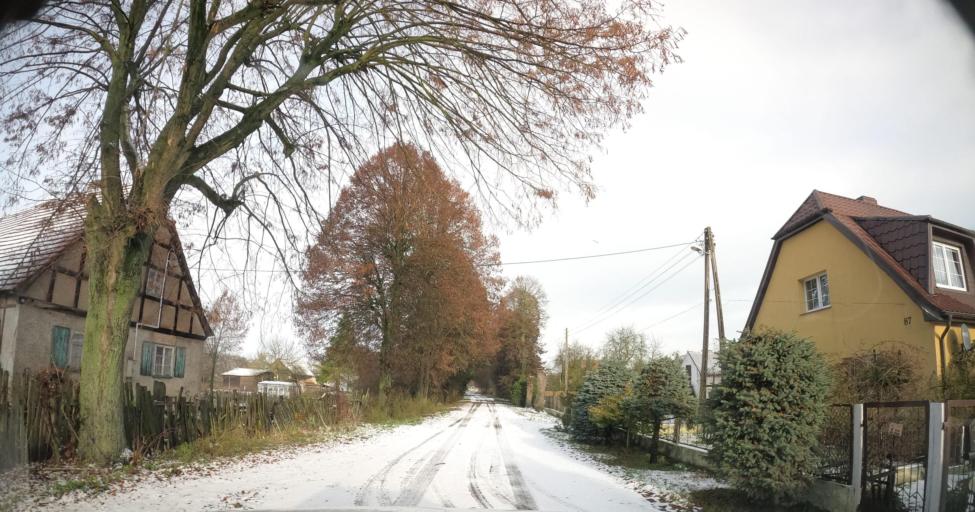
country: PL
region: West Pomeranian Voivodeship
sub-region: Powiat gryfinski
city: Mieszkowice
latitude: 52.7375
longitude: 14.4924
